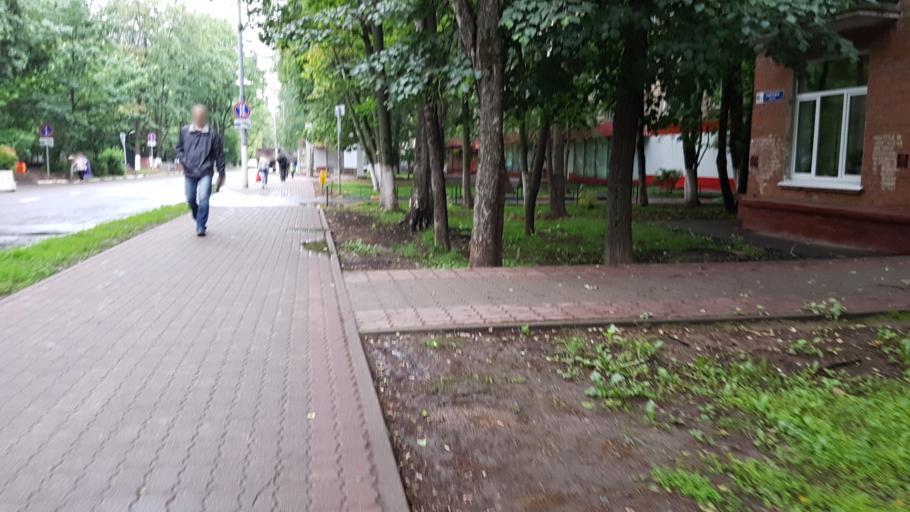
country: RU
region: Moscow
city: Khimki
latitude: 55.8898
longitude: 37.4517
